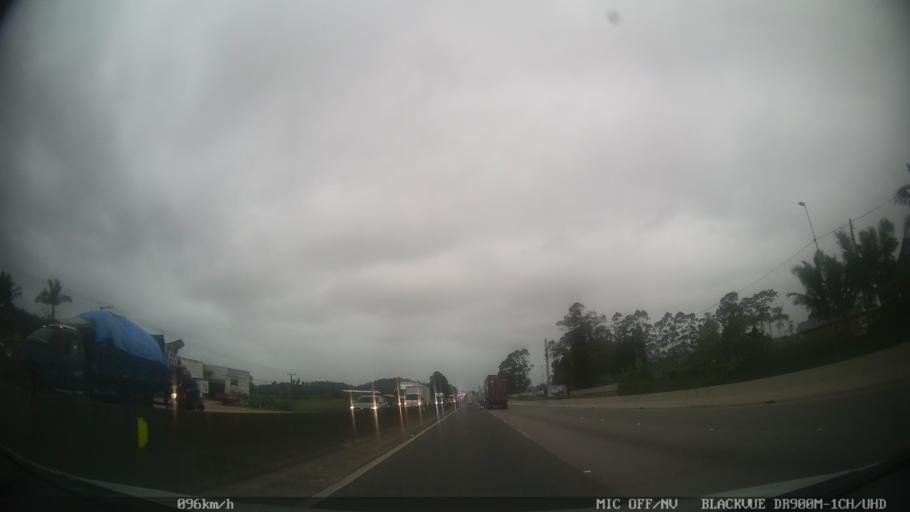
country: BR
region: Santa Catarina
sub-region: Barra Velha
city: Barra Velha
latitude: -26.6250
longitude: -48.7128
